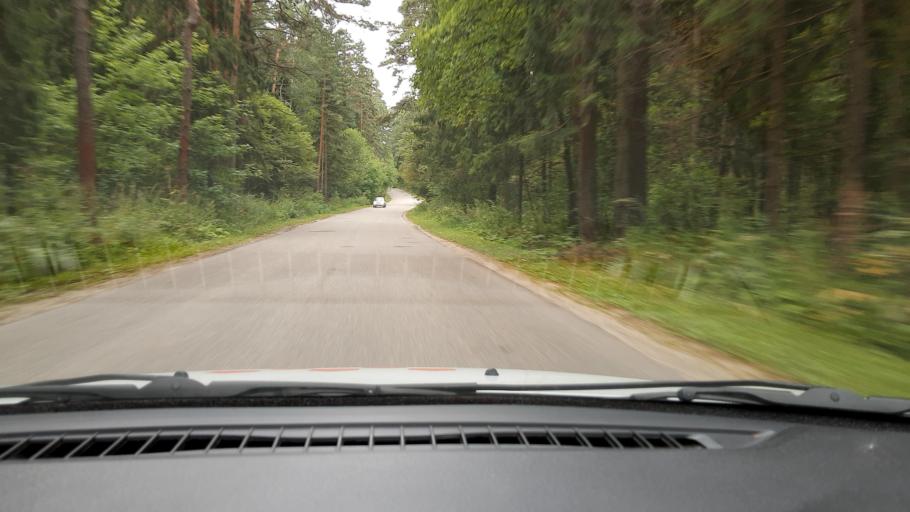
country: RU
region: Nizjnij Novgorod
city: Novaya Balakhna
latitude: 56.5925
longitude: 43.6413
